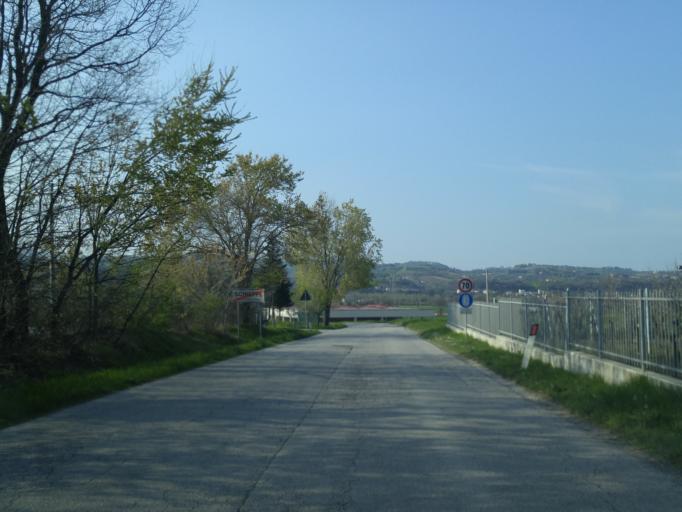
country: IT
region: The Marches
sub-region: Provincia di Pesaro e Urbino
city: Tavernelle
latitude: 43.7195
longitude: 12.8980
